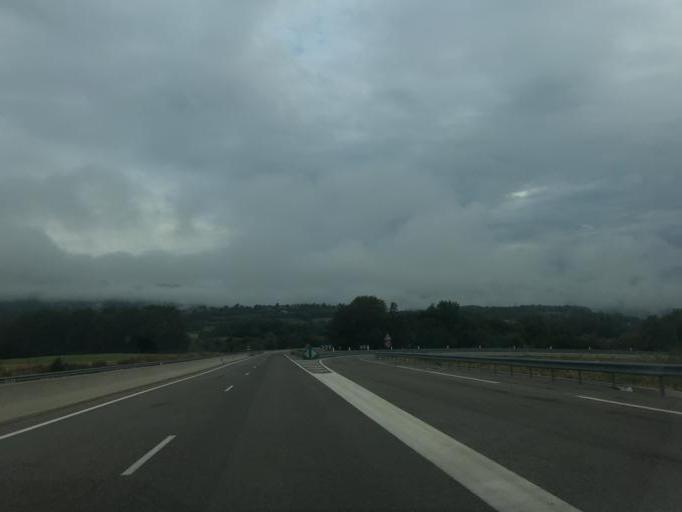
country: FR
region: Rhone-Alpes
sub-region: Departement de l'Ain
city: Dortan
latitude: 46.2939
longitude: 5.6517
